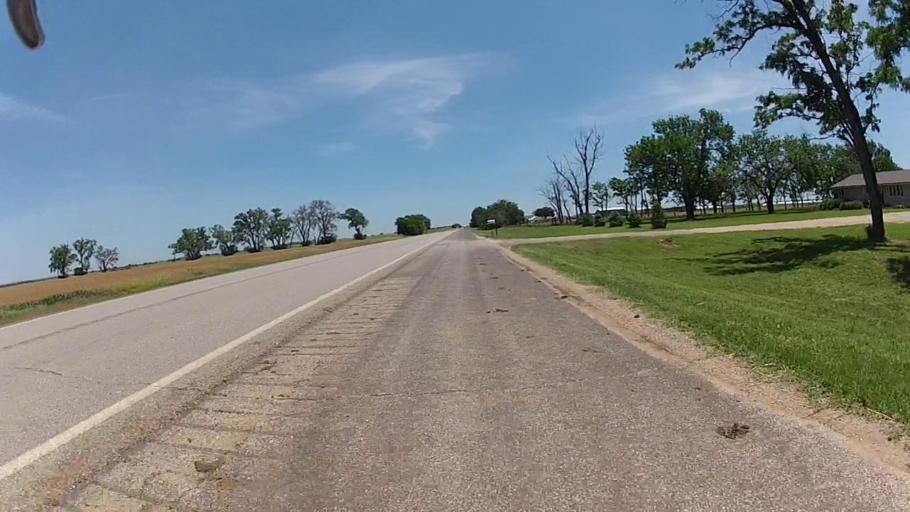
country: US
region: Kansas
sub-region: Barber County
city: Medicine Lodge
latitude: 37.2536
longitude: -98.4010
